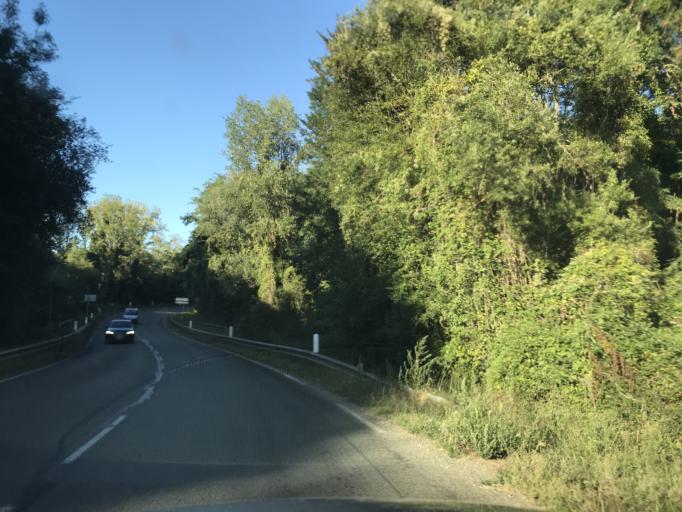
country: FR
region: Aquitaine
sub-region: Departement de la Gironde
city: Sauveterre-de-Guyenne
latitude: 44.6537
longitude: -0.1095
